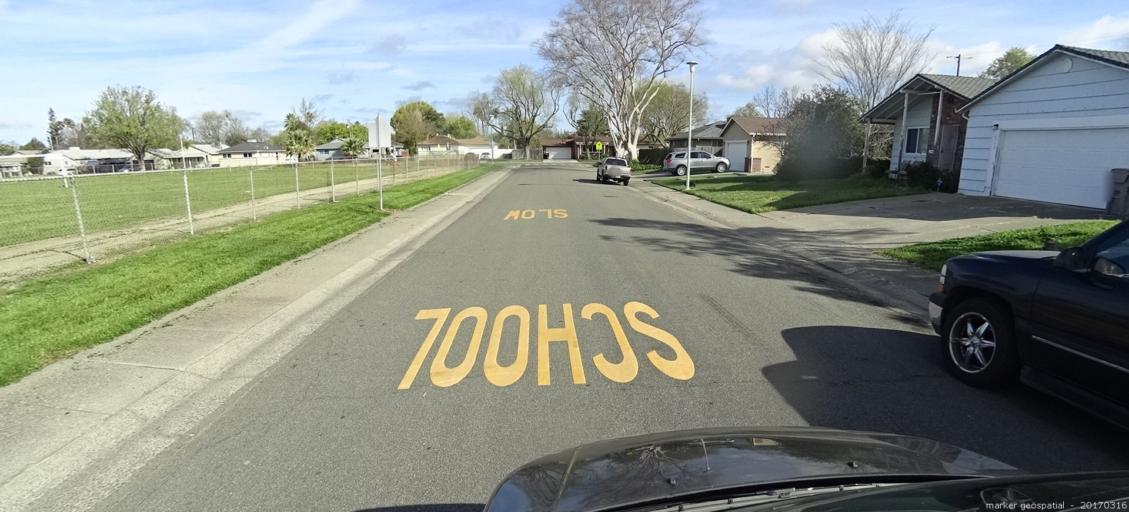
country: US
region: California
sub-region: Sacramento County
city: Parkway
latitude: 38.5035
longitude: -121.4875
